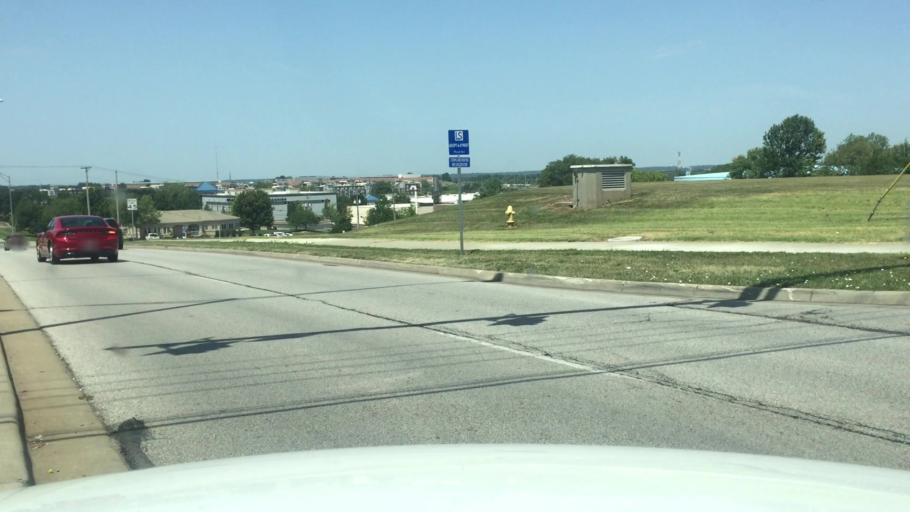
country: US
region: Missouri
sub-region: Jackson County
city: Lees Summit
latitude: 38.9251
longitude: -94.3800
